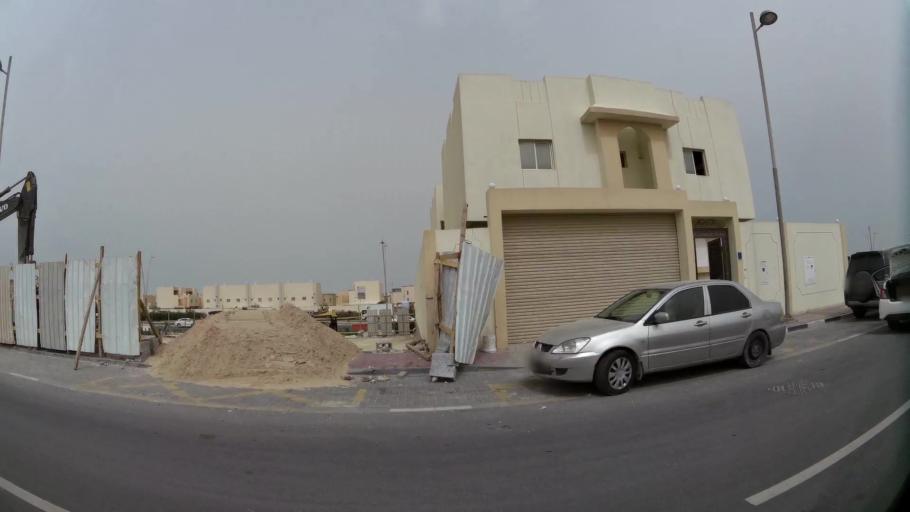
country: QA
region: Baladiyat ad Dawhah
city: Doha
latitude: 25.2300
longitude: 51.5538
